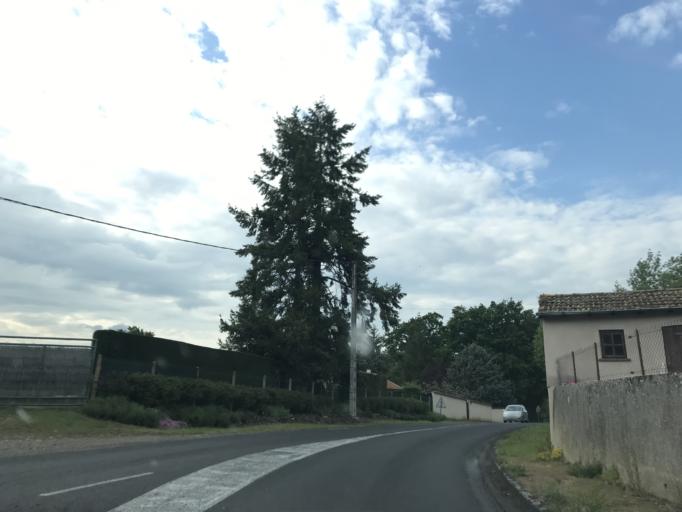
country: FR
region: Auvergne
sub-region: Departement du Puy-de-Dome
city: Orleat
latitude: 45.8944
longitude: 3.3857
